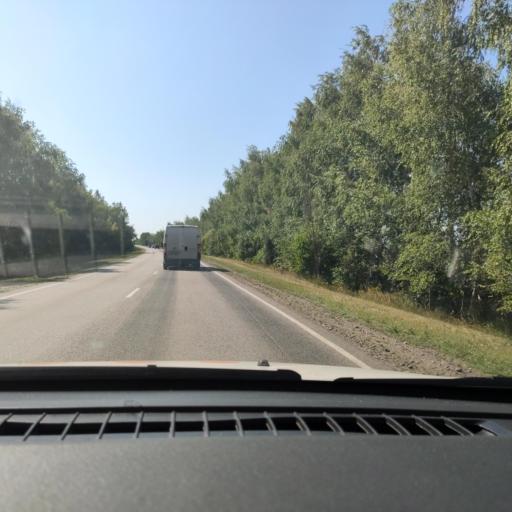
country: RU
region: Voronezj
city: Liski
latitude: 50.8012
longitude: 39.3365
